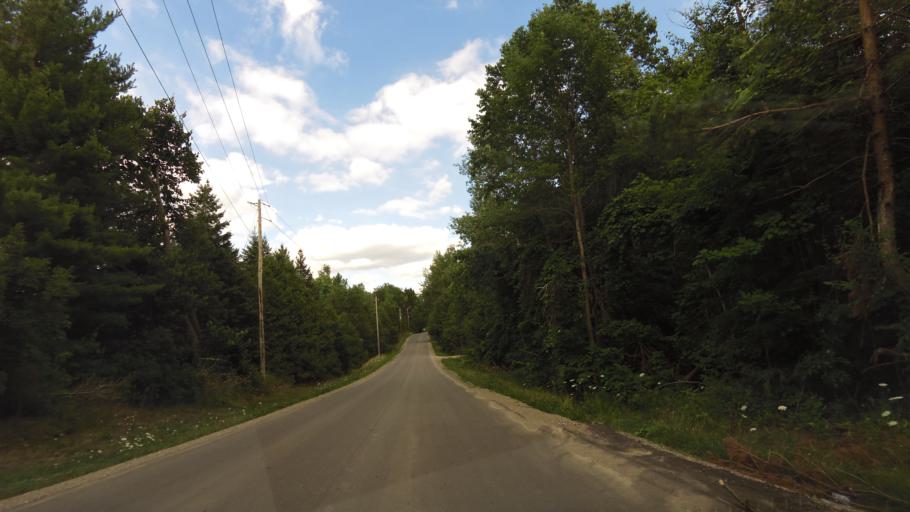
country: CA
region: Ontario
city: Orangeville
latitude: 43.9830
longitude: -79.9367
